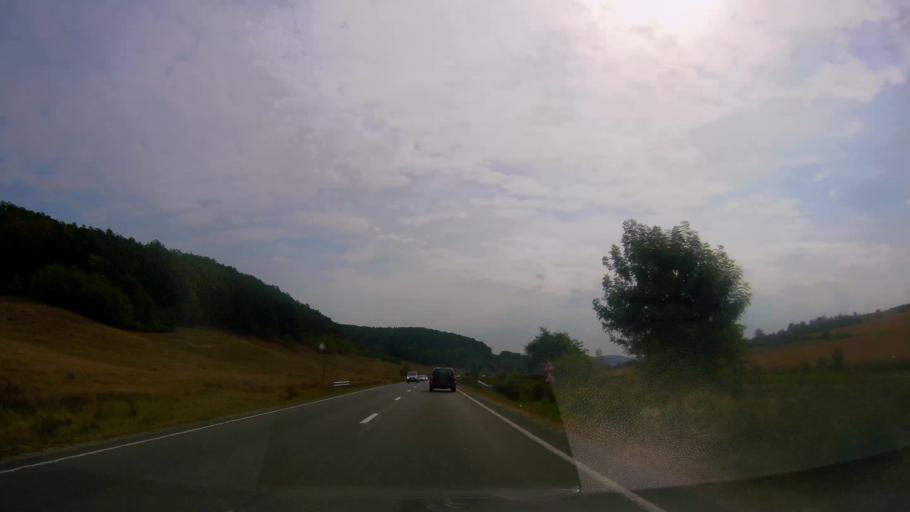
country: RO
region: Salaj
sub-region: Comuna Hida
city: Hida
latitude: 47.0547
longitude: 23.2308
